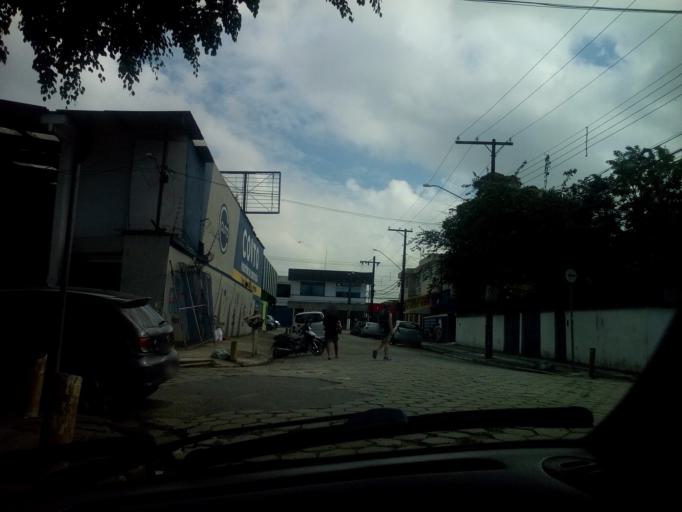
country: BR
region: Sao Paulo
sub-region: Guaruja
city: Guaruja
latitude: -23.9920
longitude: -46.2791
